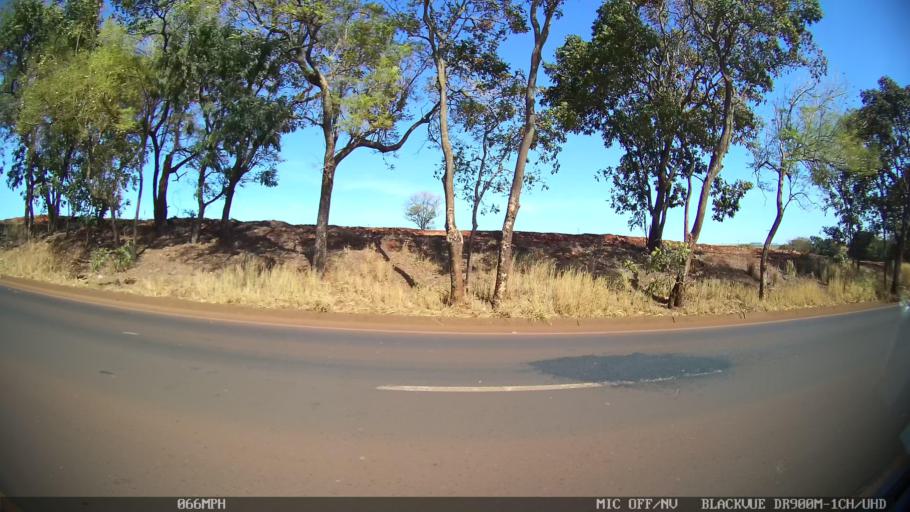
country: BR
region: Sao Paulo
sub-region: Sao Joaquim Da Barra
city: Sao Joaquim da Barra
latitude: -20.5169
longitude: -47.8806
